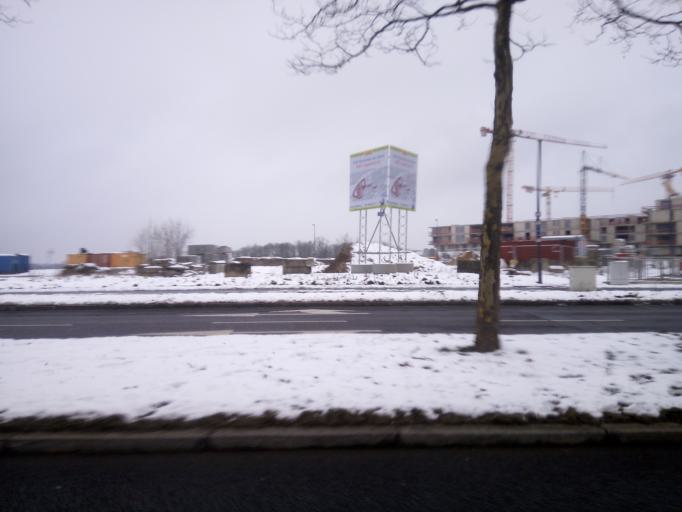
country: LU
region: Luxembourg
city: Kirchberg
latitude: 49.6329
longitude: 6.1618
